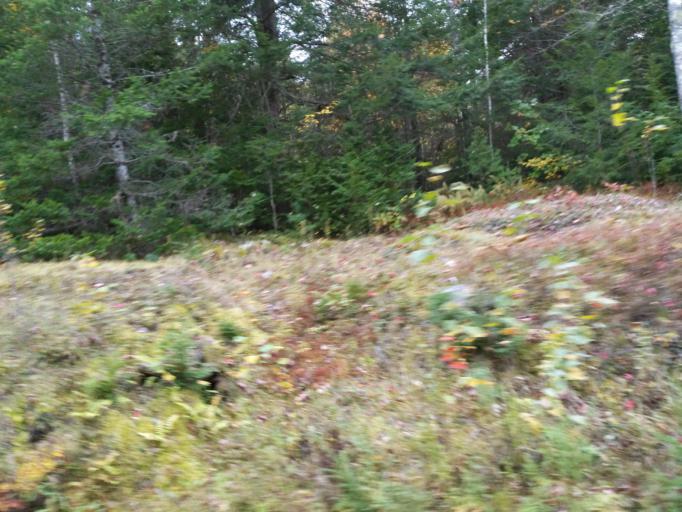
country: US
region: Maine
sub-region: Lincoln County
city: Wiscasset
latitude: 44.0673
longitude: -69.6227
